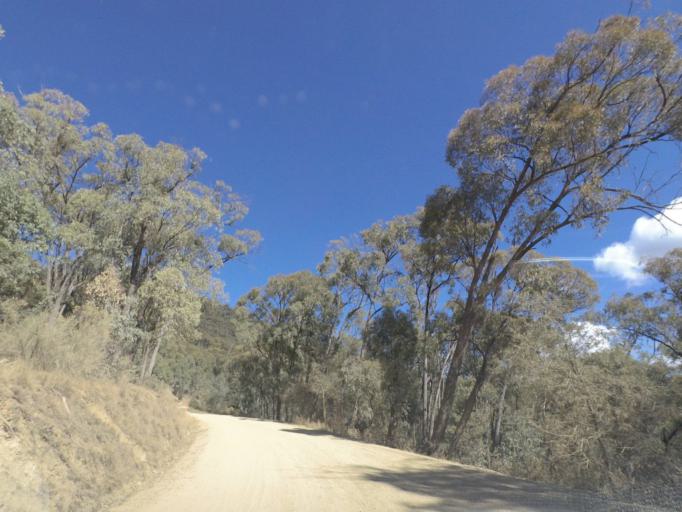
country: AU
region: Victoria
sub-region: Murrindindi
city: Alexandra
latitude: -37.3250
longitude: 145.8054
